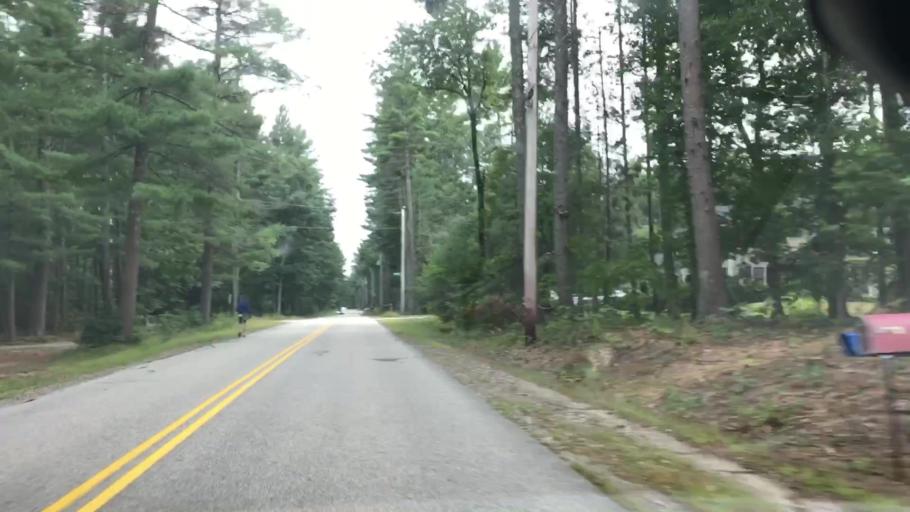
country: US
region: New Hampshire
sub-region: Hillsborough County
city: Merrimack
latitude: 42.8477
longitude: -71.5701
